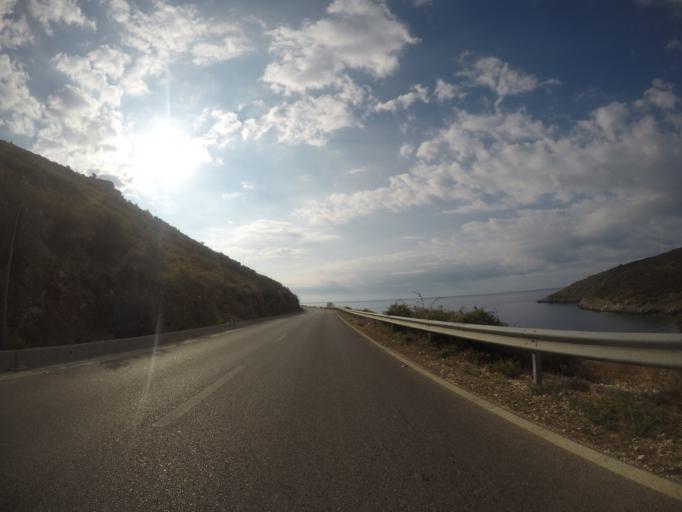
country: AL
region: Vlore
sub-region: Rrethi i Vlores
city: Himare
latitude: 40.0500
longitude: 19.8039
